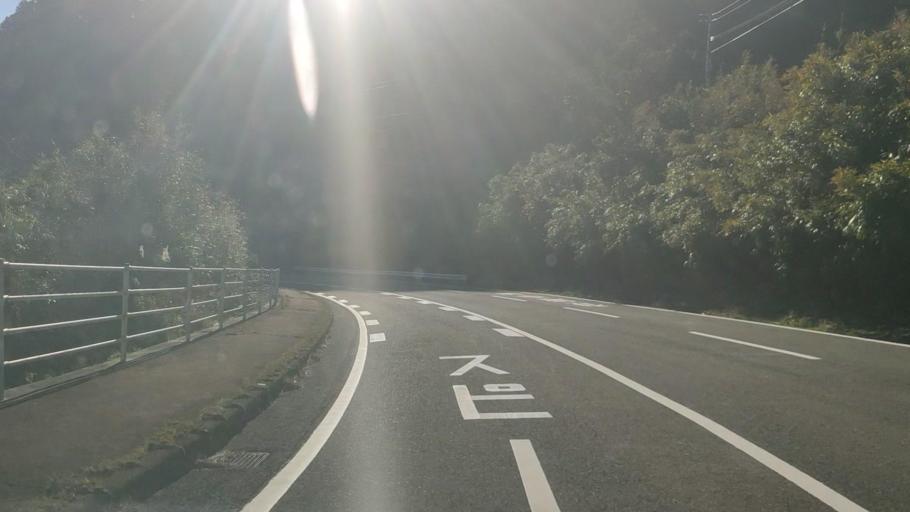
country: JP
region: Saga Prefecture
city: Kanzakimachi-kanzaki
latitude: 33.3873
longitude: 130.2616
